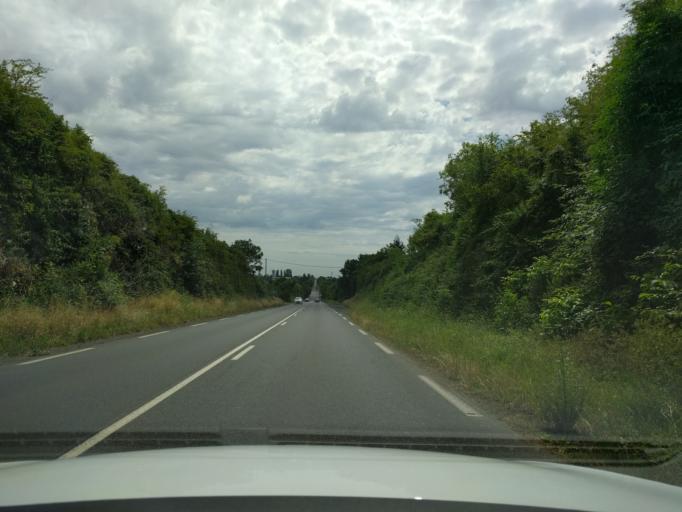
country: FR
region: Poitou-Charentes
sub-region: Departement des Deux-Sevres
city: Bessines
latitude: 46.3455
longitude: -0.5024
